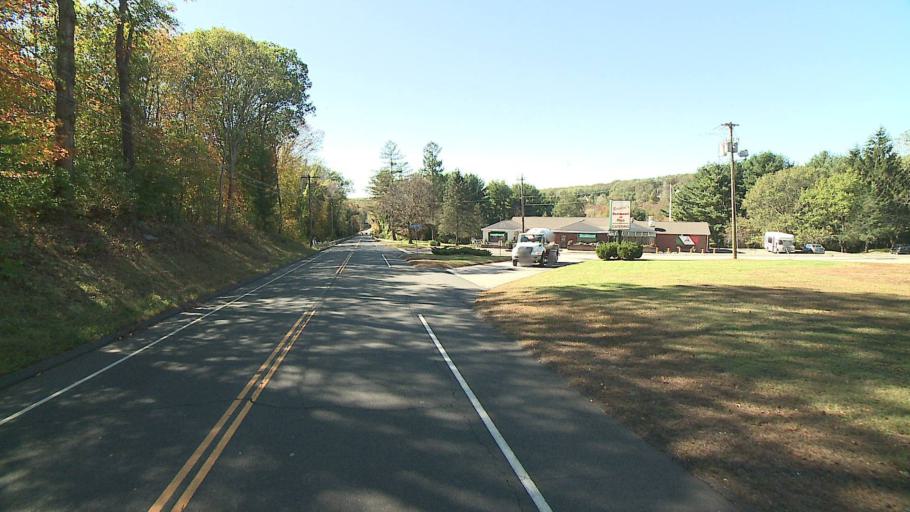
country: US
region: Connecticut
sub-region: Middlesex County
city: East Hampton
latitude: 41.5781
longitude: -72.5130
